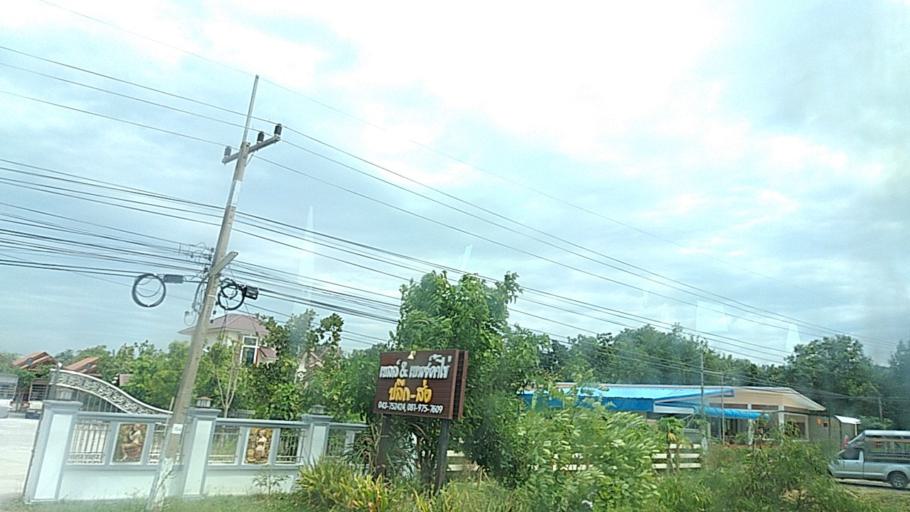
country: TH
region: Maha Sarakham
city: Chiang Yuen
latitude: 16.3420
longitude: 103.1541
